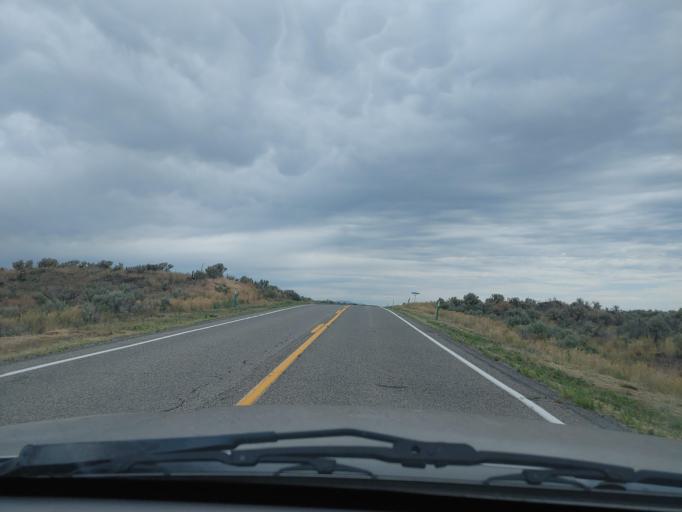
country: US
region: Idaho
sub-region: Lincoln County
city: Shoshone
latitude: 43.0909
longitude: -114.0911
